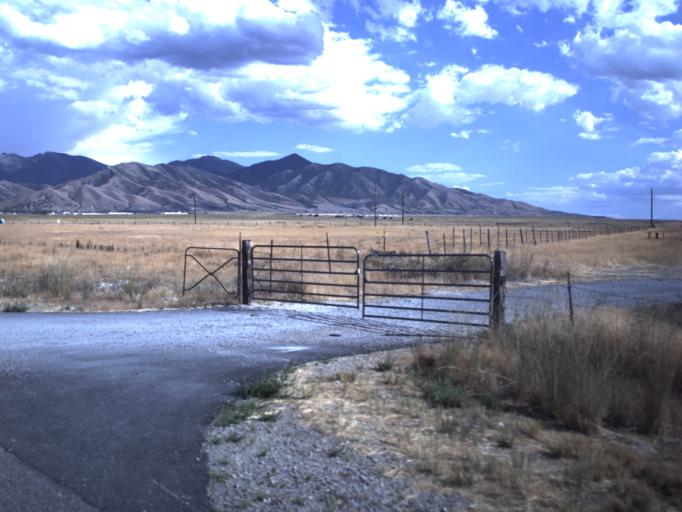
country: US
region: Utah
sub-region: Tooele County
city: Tooele
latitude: 40.5655
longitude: -112.3643
